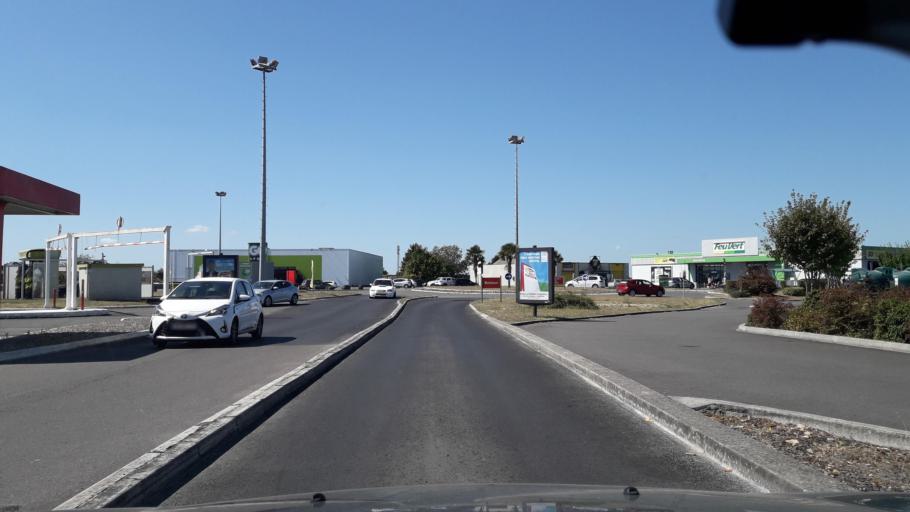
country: FR
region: Poitou-Charentes
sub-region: Departement de la Charente
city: Gond-Pontouvre
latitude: 45.6919
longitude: 0.1830
